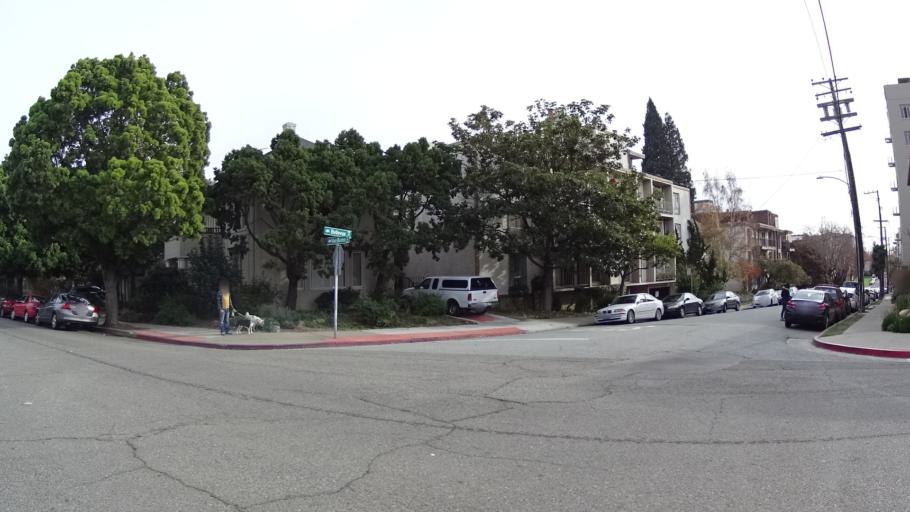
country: US
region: California
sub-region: Alameda County
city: Oakland
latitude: 37.8106
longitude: -122.2526
